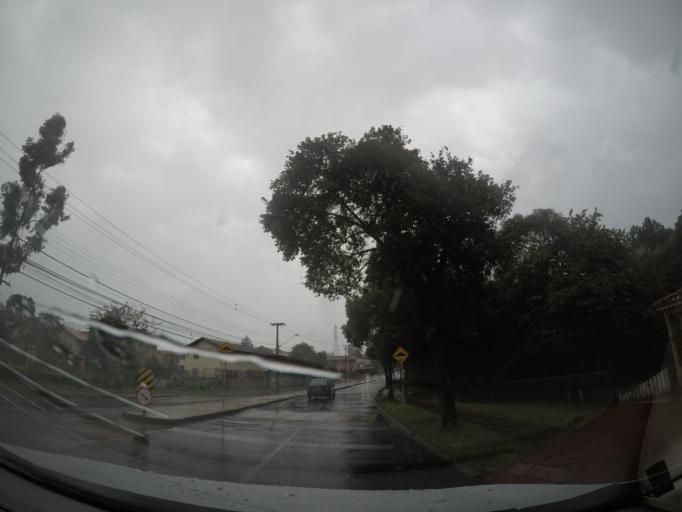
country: BR
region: Parana
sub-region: Curitiba
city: Curitiba
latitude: -25.4514
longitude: -49.3578
